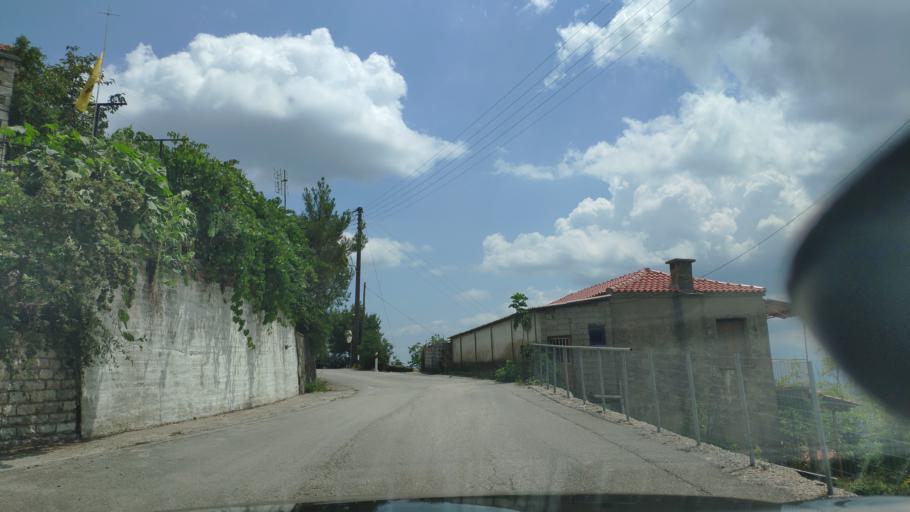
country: GR
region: Epirus
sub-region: Nomos Artas
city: Agios Dimitrios
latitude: 39.3255
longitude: 20.9981
